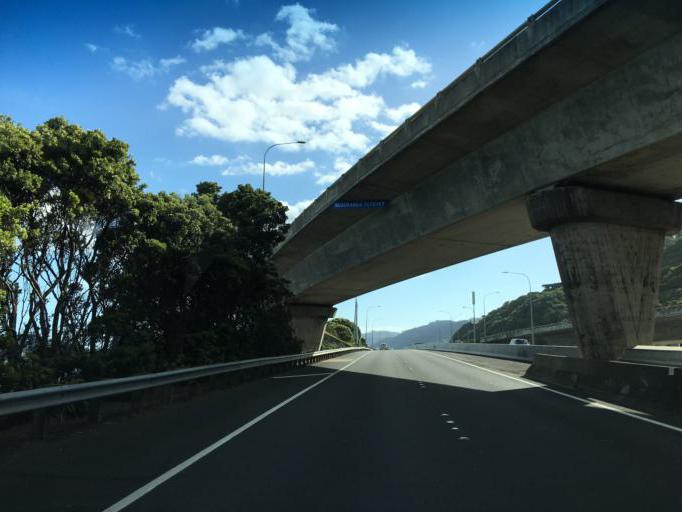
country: NZ
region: Wellington
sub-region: Wellington City
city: Wellington
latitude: -41.2470
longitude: 174.8151
